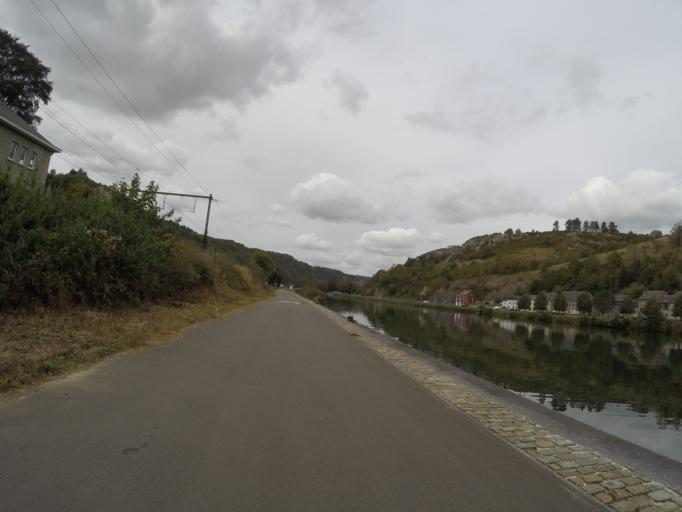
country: BE
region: Wallonia
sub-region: Province de Namur
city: Dinant
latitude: 50.2716
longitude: 4.9009
